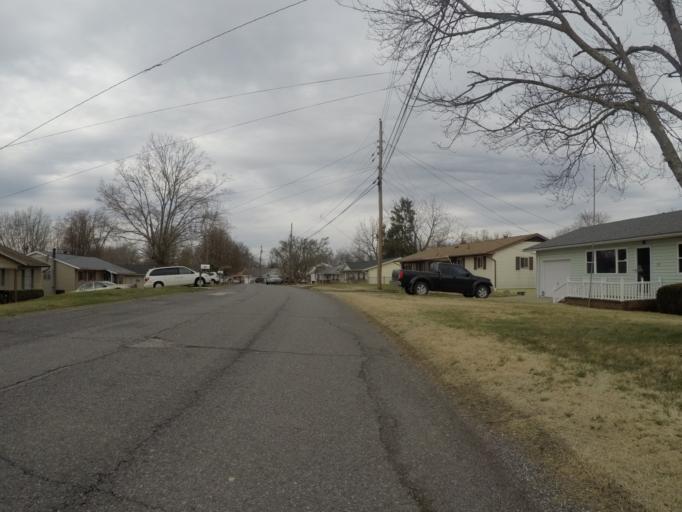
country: US
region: West Virginia
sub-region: Cabell County
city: Pea Ridge
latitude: 38.3940
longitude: -82.3784
